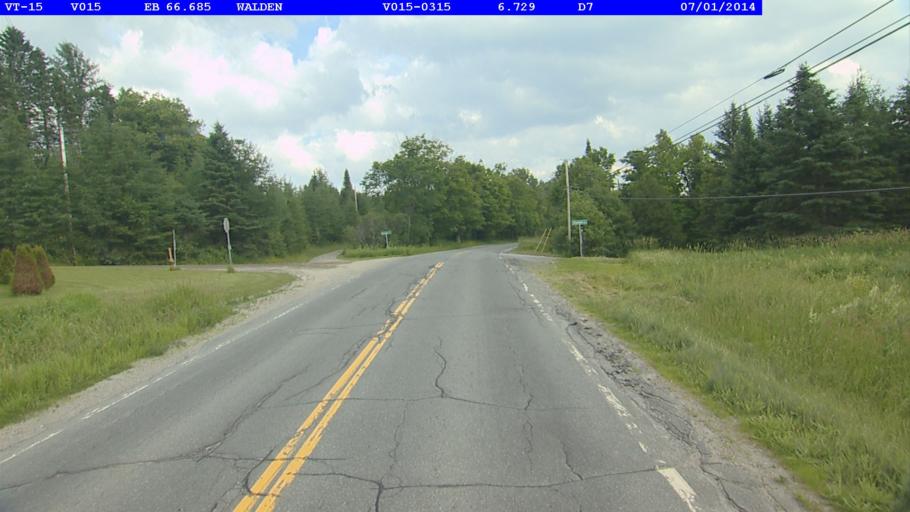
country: US
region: Vermont
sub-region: Caledonia County
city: Hardwick
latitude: 44.4289
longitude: -72.2196
